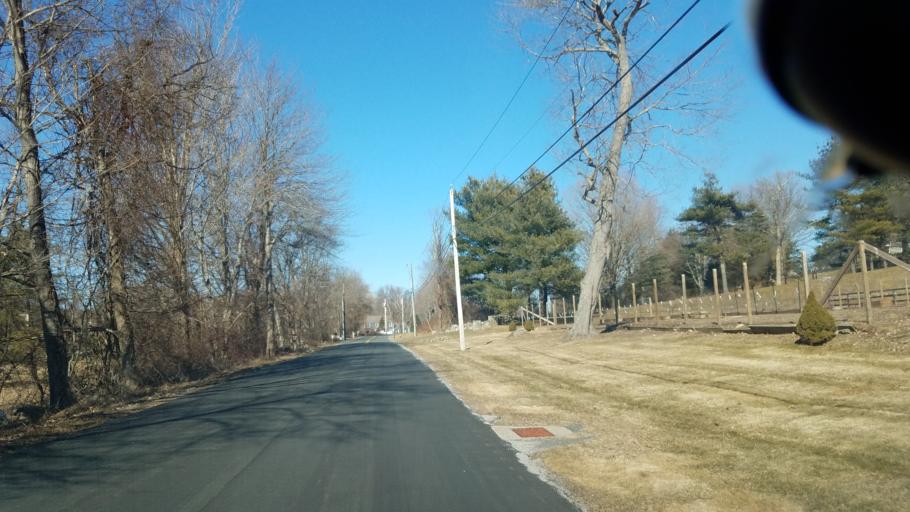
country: US
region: Connecticut
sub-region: Fairfield County
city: Newtown
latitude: 41.3601
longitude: -73.3117
